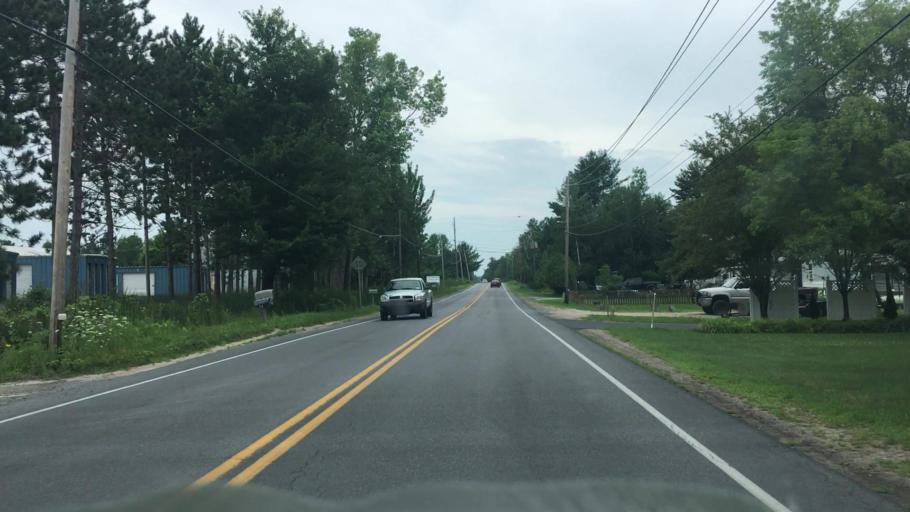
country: US
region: New York
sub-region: Clinton County
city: Plattsburgh West
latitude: 44.6653
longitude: -73.5081
